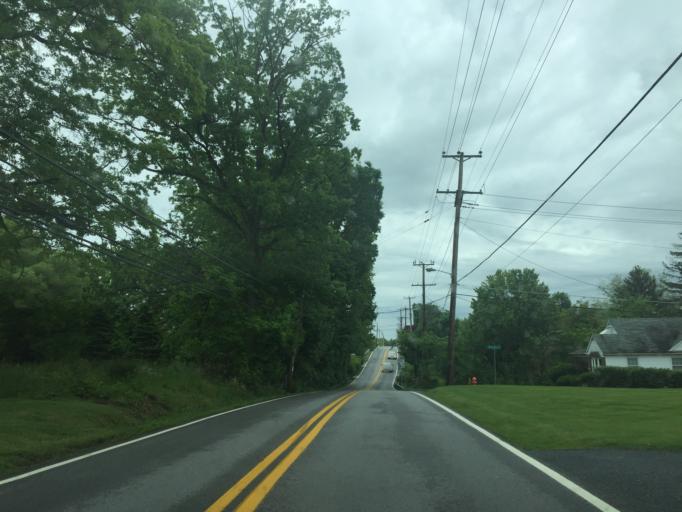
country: US
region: Maryland
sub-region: Baltimore County
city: Perry Hall
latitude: 39.4077
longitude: -76.4562
